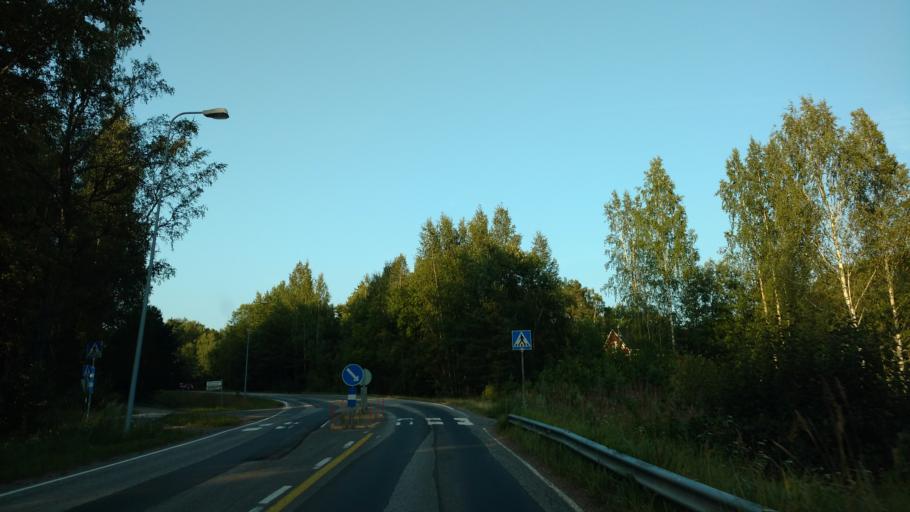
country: FI
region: Varsinais-Suomi
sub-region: Aboland-Turunmaa
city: Dragsfjaerd
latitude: 60.0723
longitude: 22.4840
